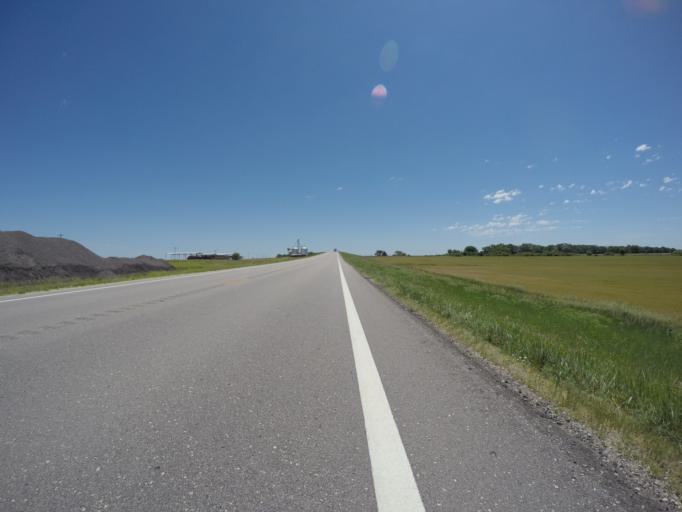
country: US
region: Kansas
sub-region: Republic County
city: Belleville
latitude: 39.8126
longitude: -97.7197
